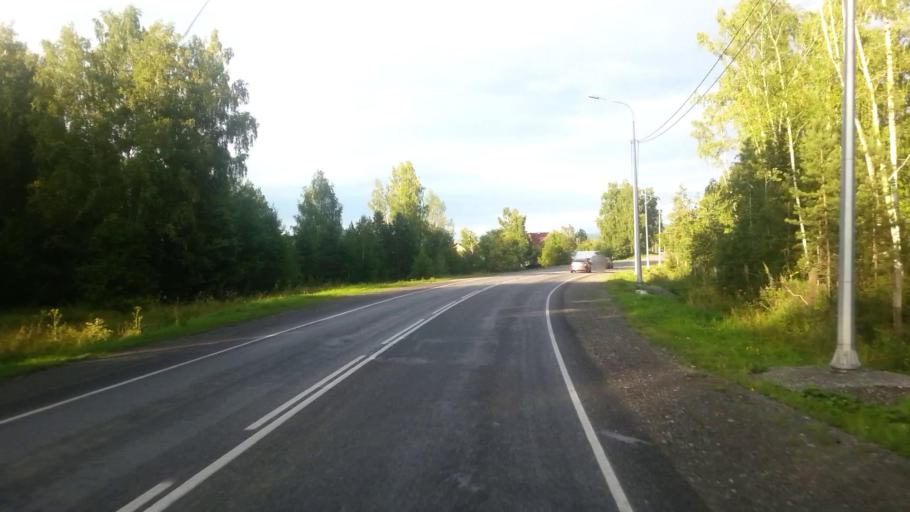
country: RU
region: Altay
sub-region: Mayminskiy Rayon
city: Manzherok
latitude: 51.8688
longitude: 85.7764
